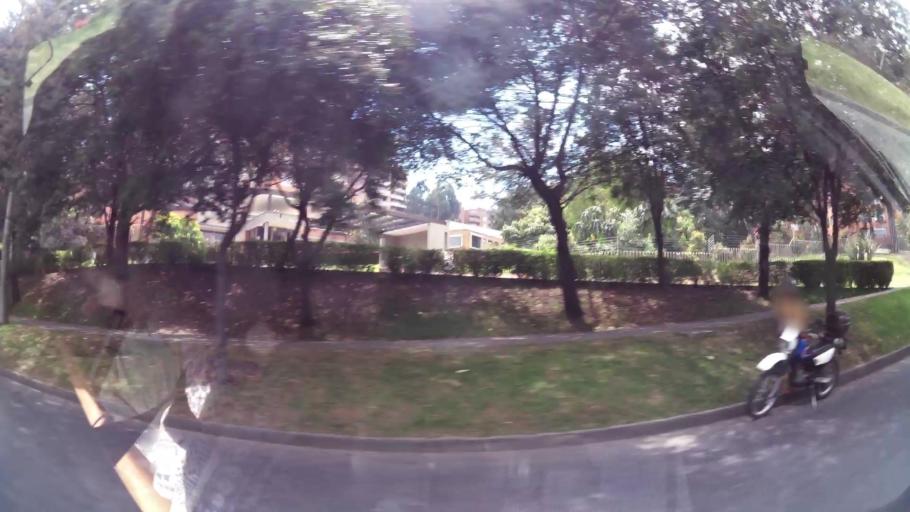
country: CO
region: Bogota D.C.
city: Barrio San Luis
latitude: 4.7195
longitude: -74.0274
